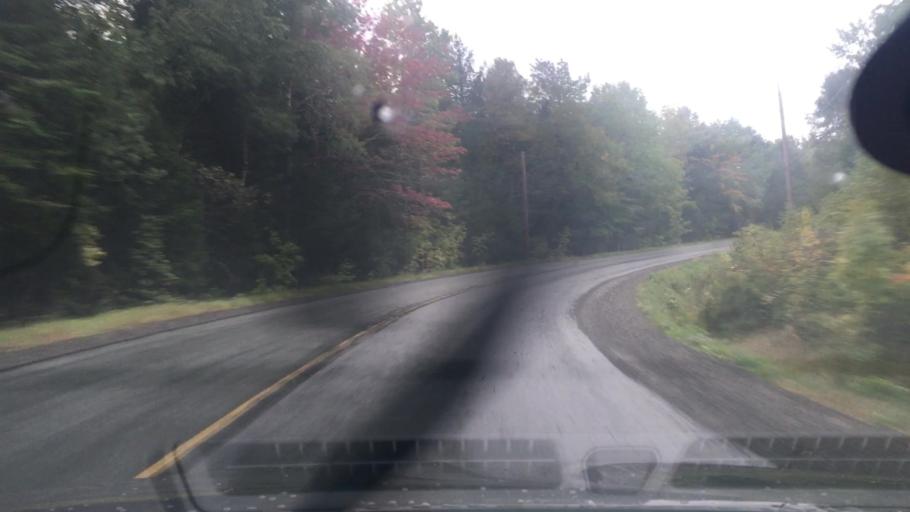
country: CA
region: Nova Scotia
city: Windsor
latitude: 44.8373
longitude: -64.2506
